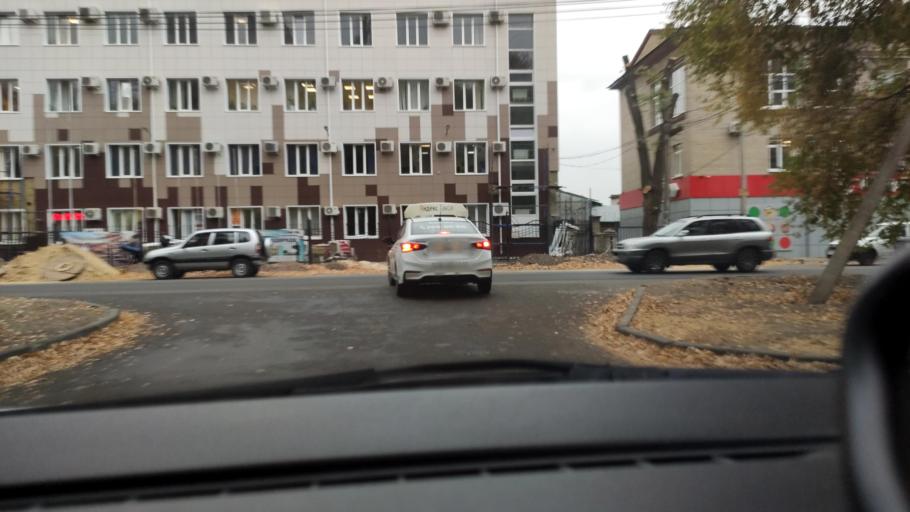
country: RU
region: Voronezj
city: Voronezh
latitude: 51.6868
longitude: 39.1880
